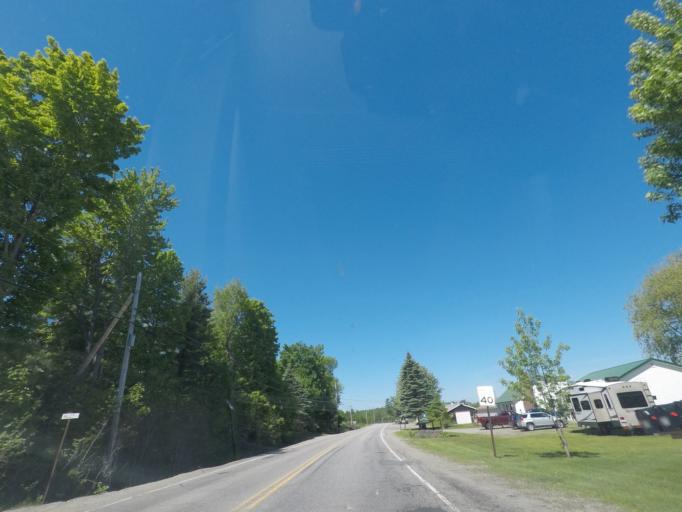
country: US
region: Maine
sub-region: Kennebec County
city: Gardiner
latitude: 44.2309
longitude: -69.8042
